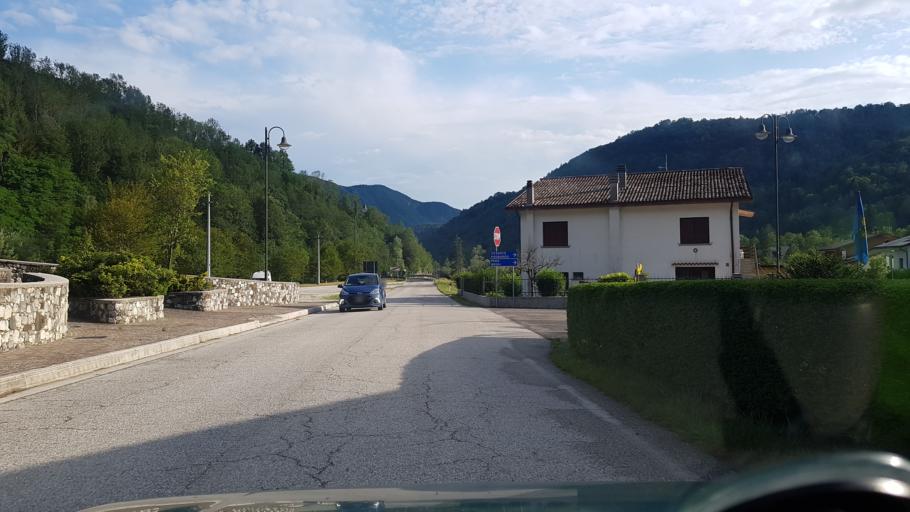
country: IT
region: Friuli Venezia Giulia
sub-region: Provincia di Udine
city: Lusevera
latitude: 46.2790
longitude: 13.2615
